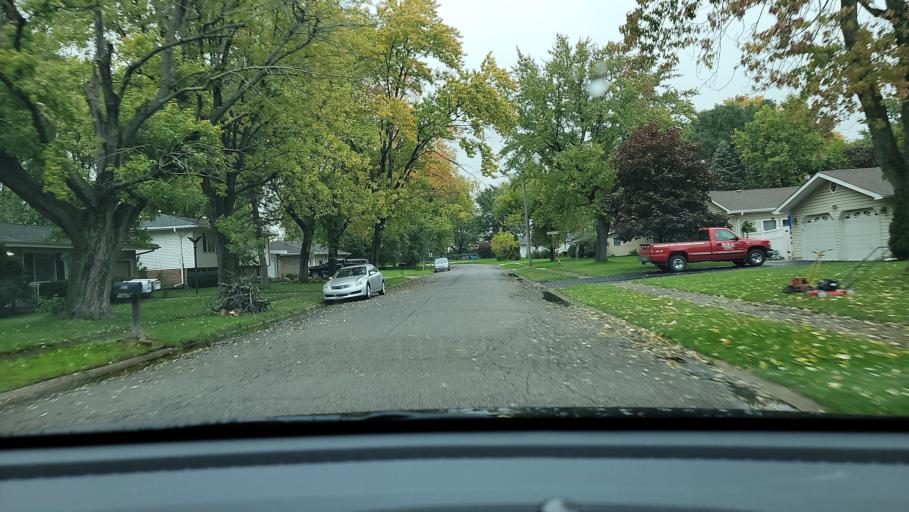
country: US
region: Indiana
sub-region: Porter County
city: Portage
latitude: 41.5739
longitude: -87.1727
